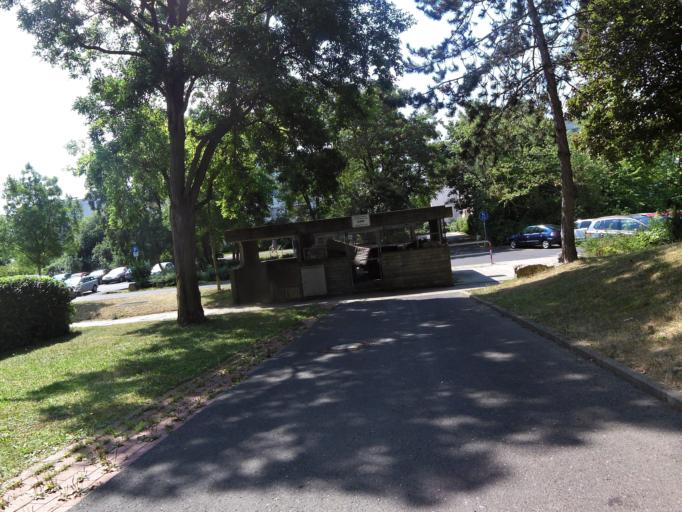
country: DE
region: Bavaria
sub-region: Regierungsbezirk Unterfranken
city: Randersacker
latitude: 49.7487
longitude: 9.9599
